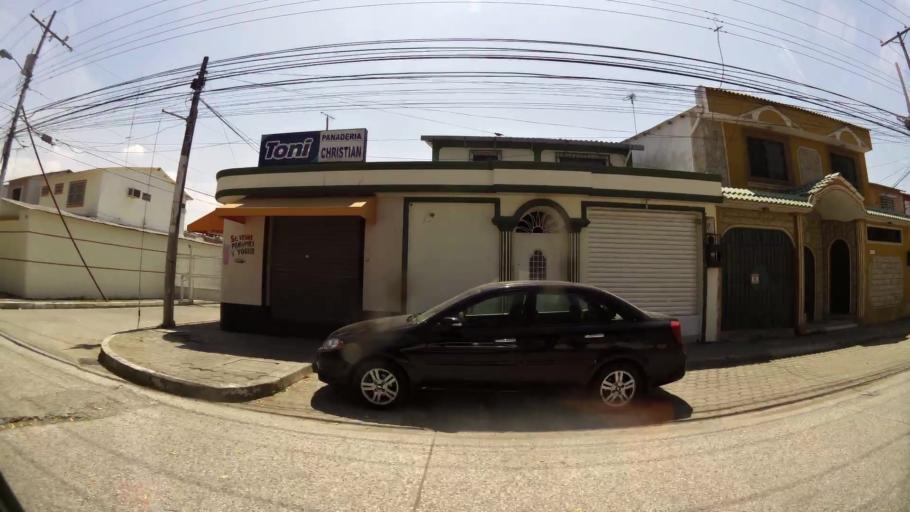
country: EC
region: Guayas
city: Eloy Alfaro
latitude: -2.1108
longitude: -79.9053
